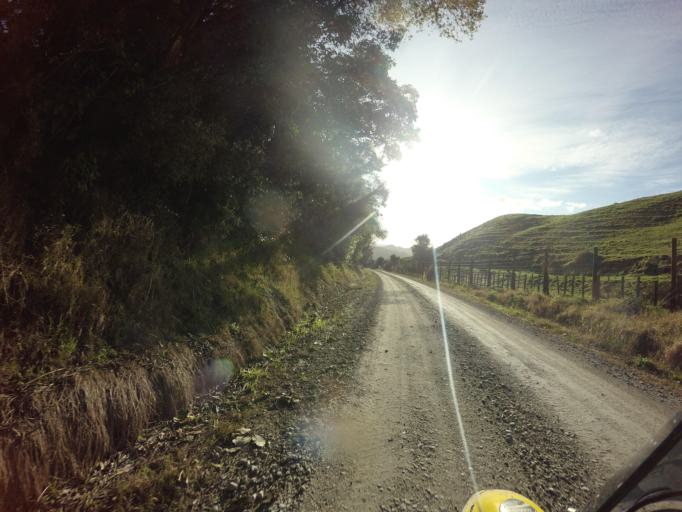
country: NZ
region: Hawke's Bay
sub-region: Wairoa District
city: Wairoa
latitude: -38.7518
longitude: 177.5396
